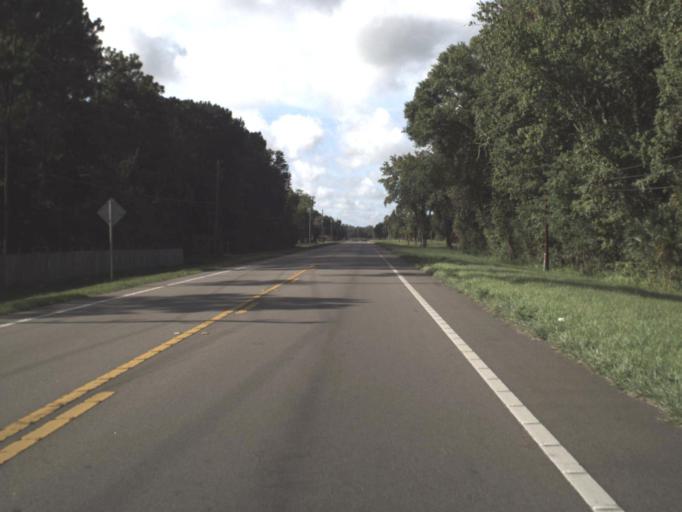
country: US
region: Florida
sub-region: Pasco County
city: Shady Hills
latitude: 28.3507
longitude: -82.5042
